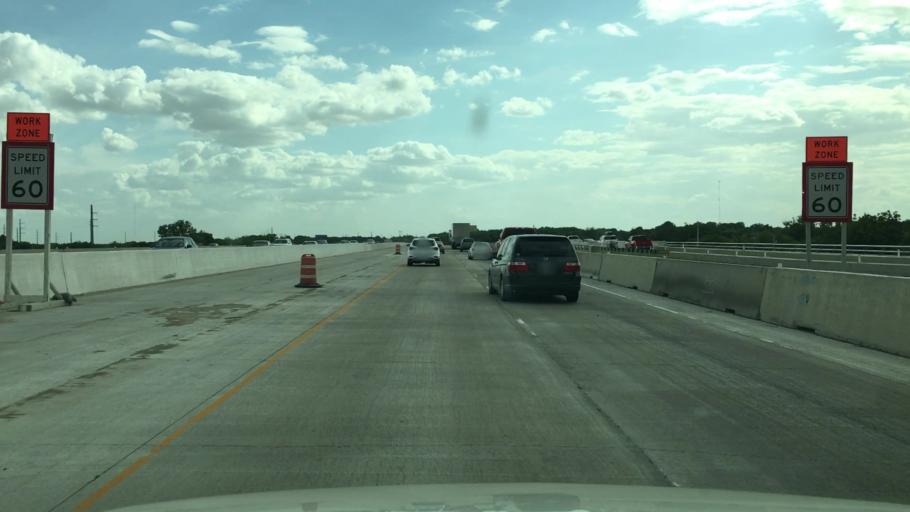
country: US
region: Texas
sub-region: McLennan County
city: Bruceville-Eddy
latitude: 31.3216
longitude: -97.2338
